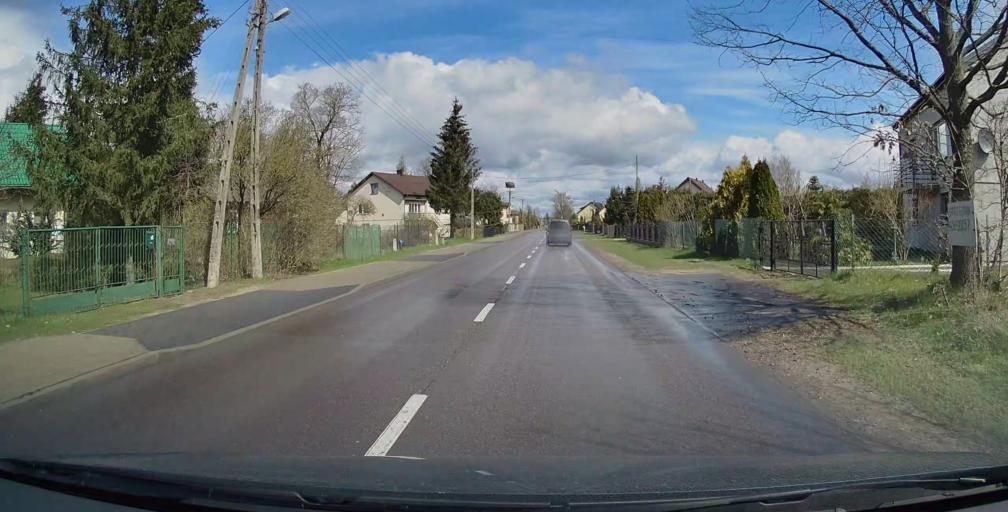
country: PL
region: Masovian Voivodeship
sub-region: Powiat wyszkowski
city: Dlugosiodlo
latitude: 52.7017
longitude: 21.6058
